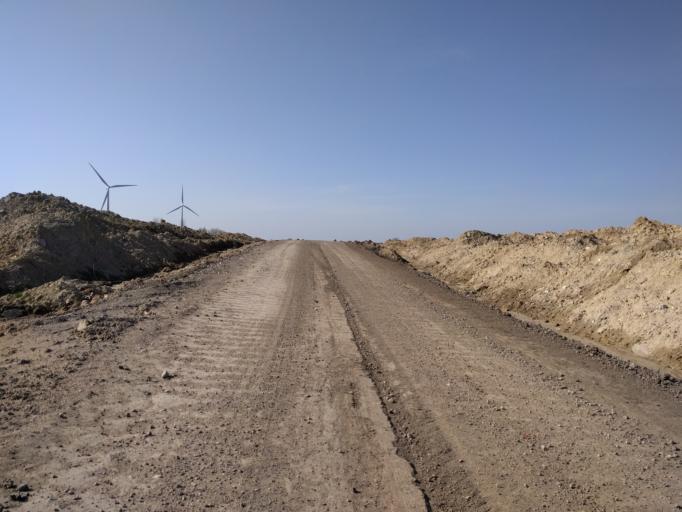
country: DK
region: South Denmark
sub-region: Kerteminde Kommune
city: Munkebo
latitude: 55.4589
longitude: 10.5230
